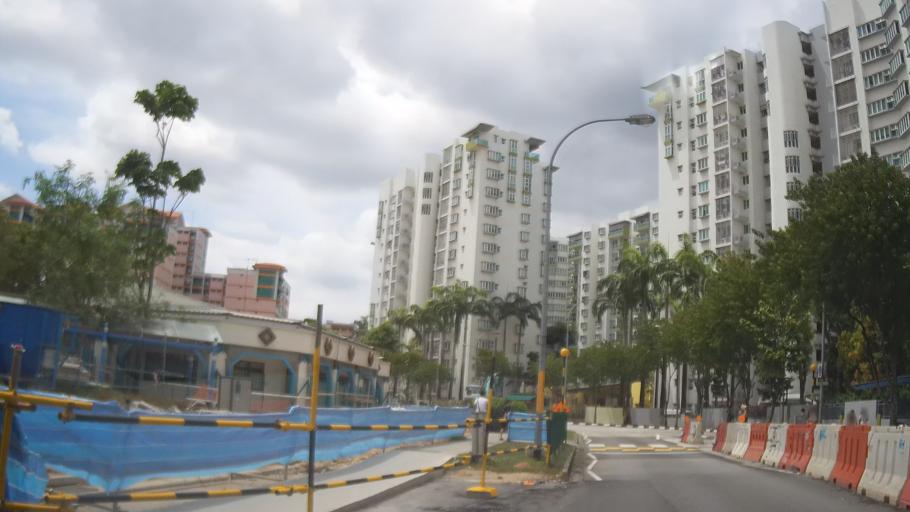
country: MY
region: Johor
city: Johor Bahru
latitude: 1.3863
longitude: 103.7442
